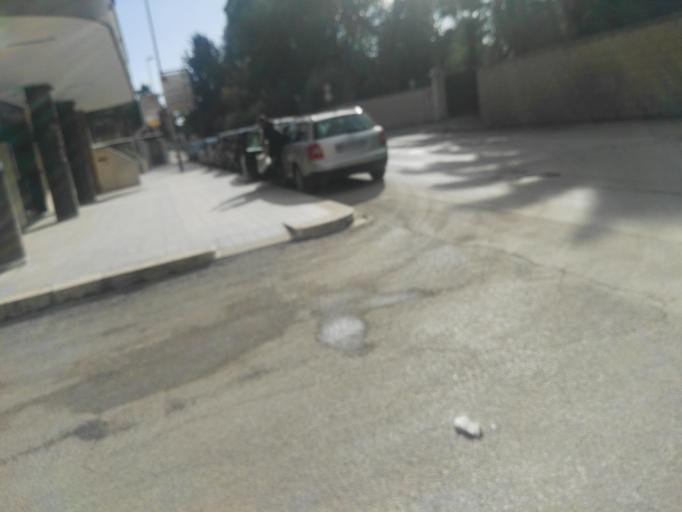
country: IT
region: Apulia
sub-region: Provincia di Barletta - Andria - Trani
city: Andria
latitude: 41.2188
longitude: 16.3069
